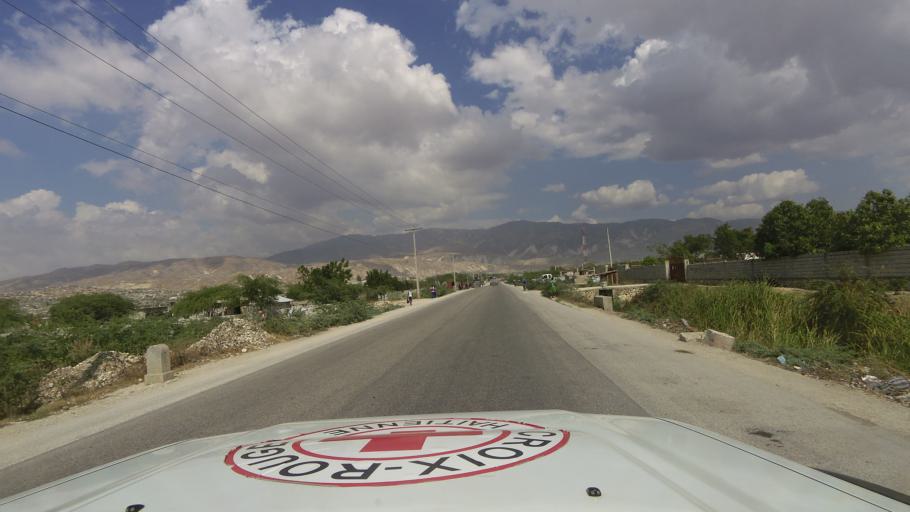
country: HT
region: Ouest
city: Croix des Bouquets
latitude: 18.6431
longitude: -72.2616
